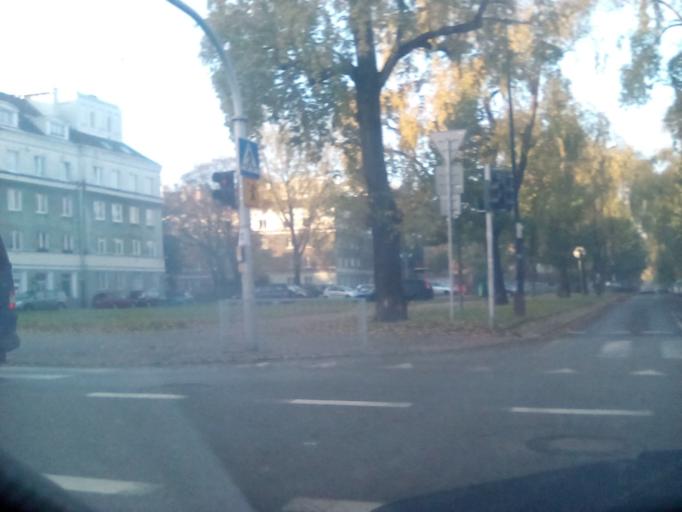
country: PL
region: Masovian Voivodeship
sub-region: Warszawa
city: Mokotow
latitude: 52.1991
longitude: 21.0184
